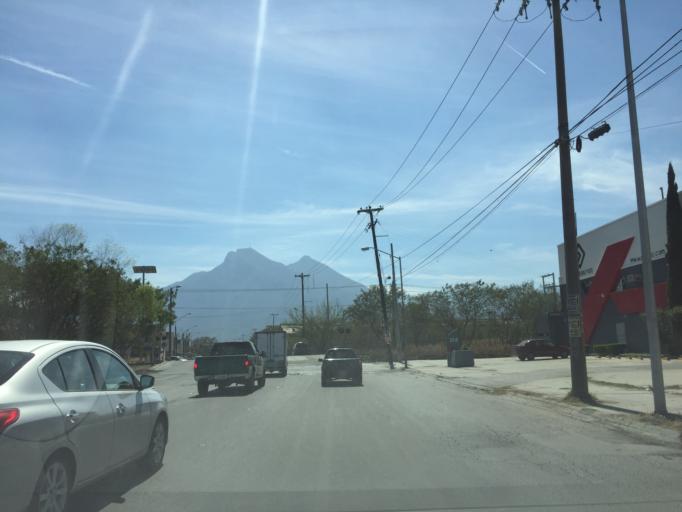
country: MX
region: Nuevo Leon
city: Guadalupe
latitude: 25.6995
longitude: -100.2400
